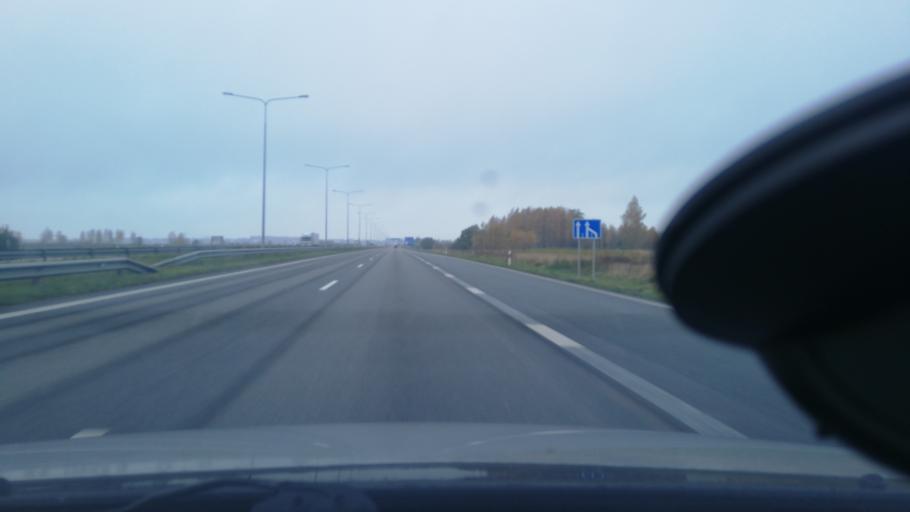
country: LT
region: Klaipedos apskritis
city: Gargzdai
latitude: 55.7127
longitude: 21.2646
